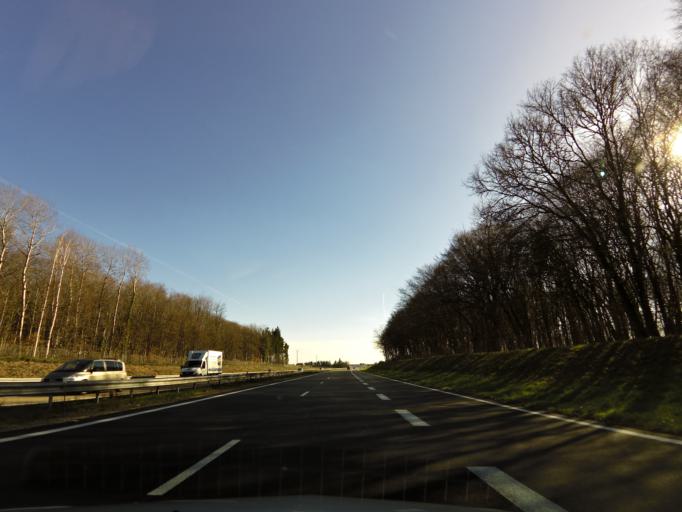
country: FR
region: Bourgogne
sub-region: Departement de l'Yonne
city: Joux-la-Ville
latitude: 47.6798
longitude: 3.8581
